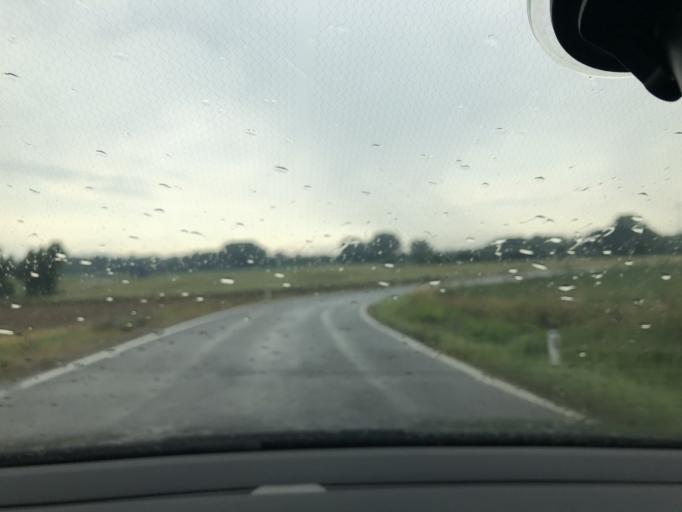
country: AT
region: Lower Austria
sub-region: Politischer Bezirk Ganserndorf
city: Ganserndorf
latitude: 48.3622
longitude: 16.6847
